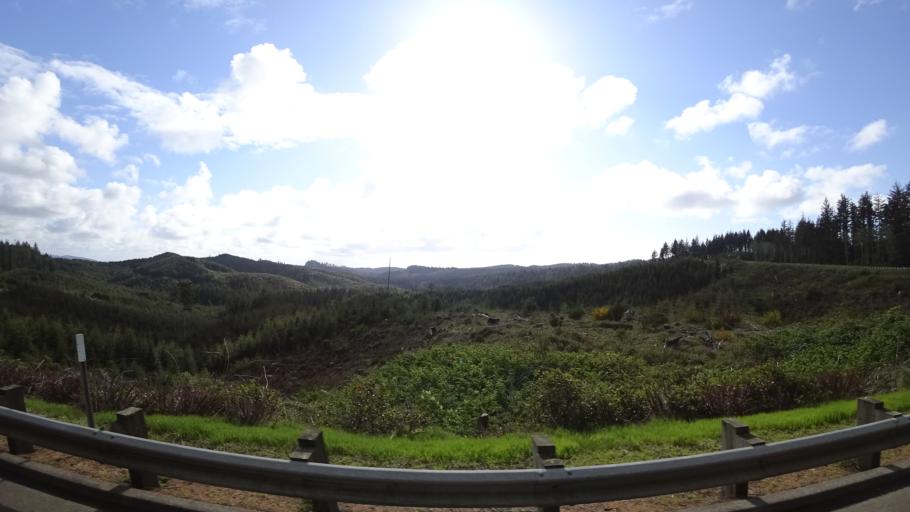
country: US
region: Oregon
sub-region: Douglas County
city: Reedsport
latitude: 43.7608
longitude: -124.1230
